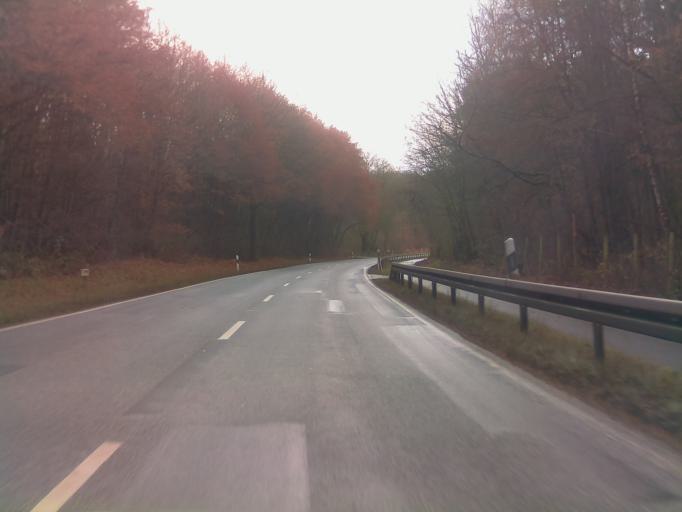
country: DE
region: Hesse
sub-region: Regierungsbezirk Giessen
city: Lich
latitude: 50.5318
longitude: 8.7761
